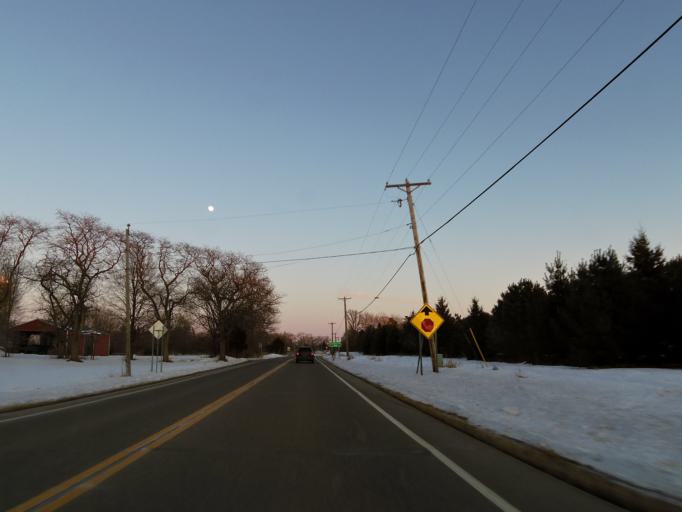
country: US
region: Minnesota
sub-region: Washington County
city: Grant
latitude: 45.0848
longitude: -92.9277
